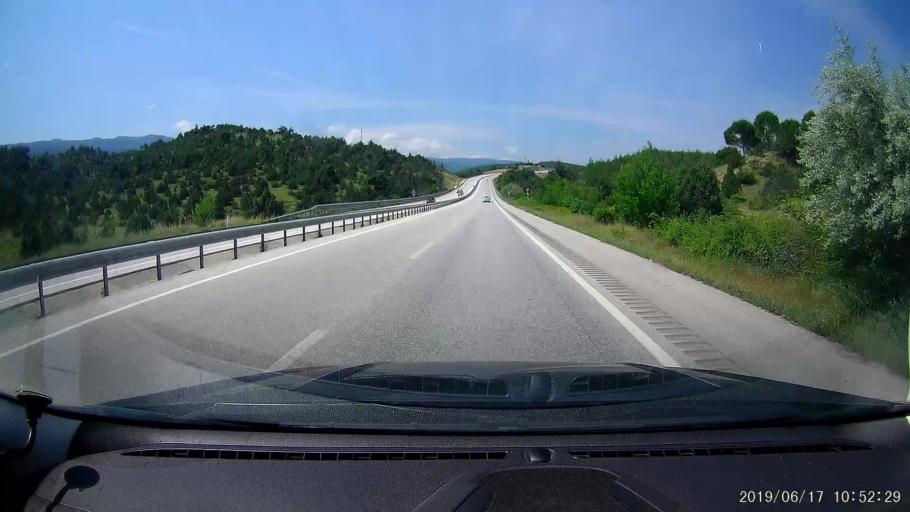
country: TR
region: Corum
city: Hacihamza
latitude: 41.0885
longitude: 34.3414
